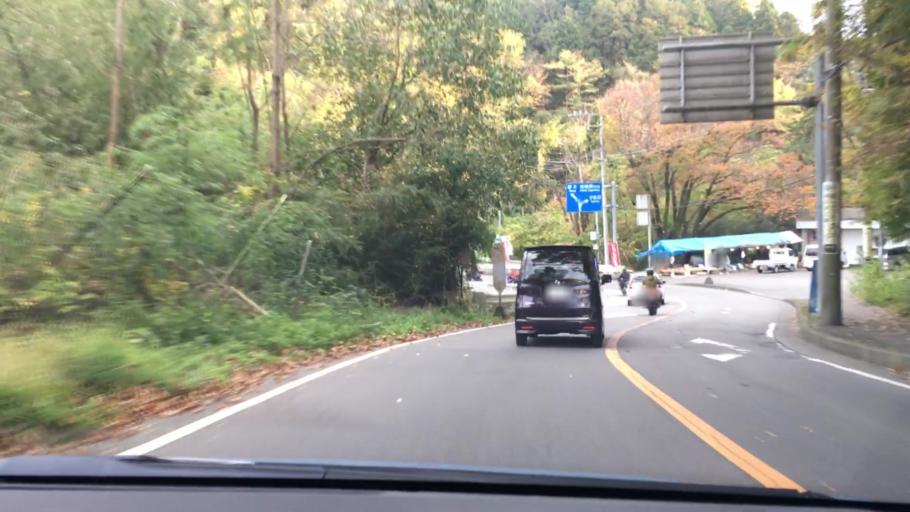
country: JP
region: Yamanashi
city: Uenohara
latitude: 35.5633
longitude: 139.2068
